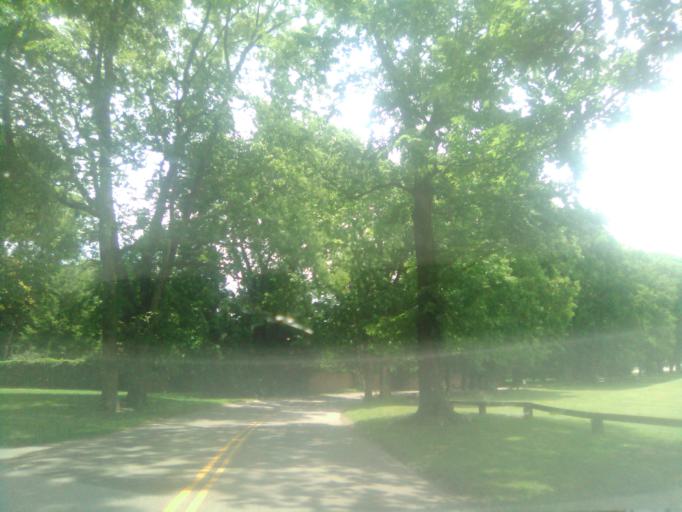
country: US
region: Tennessee
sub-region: Davidson County
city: Belle Meade
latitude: 36.0849
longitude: -86.8674
